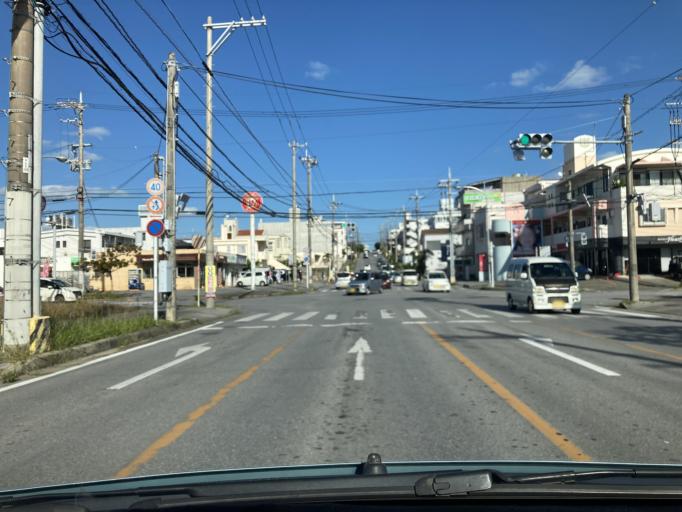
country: JP
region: Okinawa
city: Okinawa
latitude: 26.3438
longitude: 127.8266
